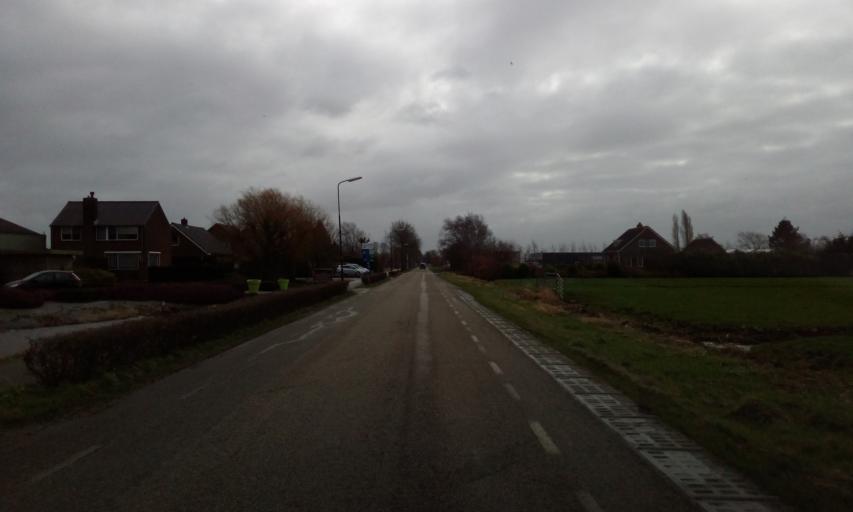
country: NL
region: Utrecht
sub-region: Gemeente De Ronde Venen
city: Mijdrecht
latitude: 52.2062
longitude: 4.8409
